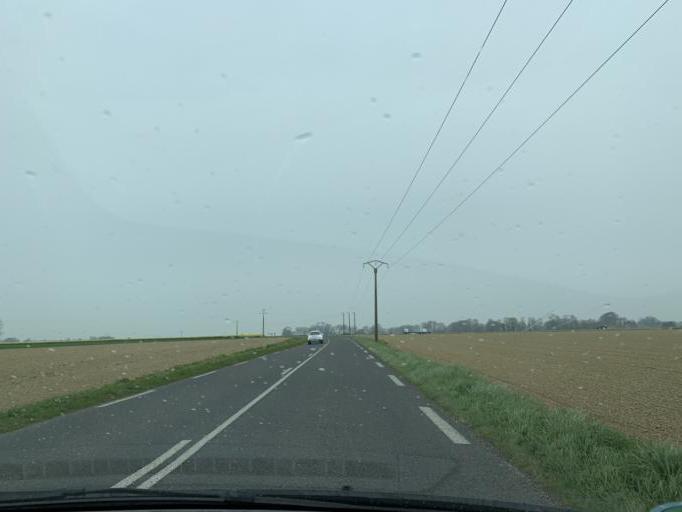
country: FR
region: Haute-Normandie
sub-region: Departement de la Seine-Maritime
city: Cany-Barville
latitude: 49.7932
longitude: 0.6612
